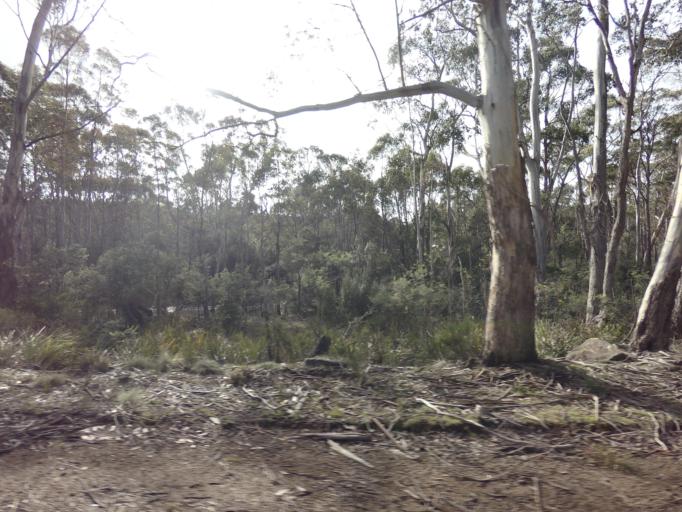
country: AU
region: Tasmania
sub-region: Derwent Valley
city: New Norfolk
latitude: -42.7610
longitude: 146.8936
